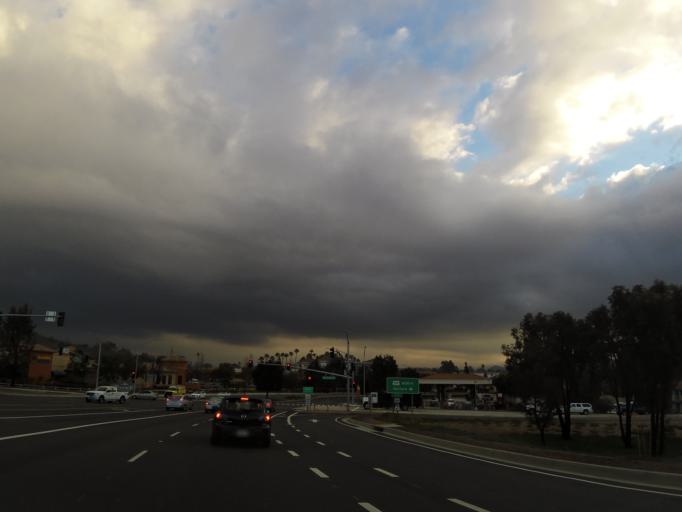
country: US
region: California
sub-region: Ventura County
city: Casa Conejo
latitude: 34.1903
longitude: -118.9386
